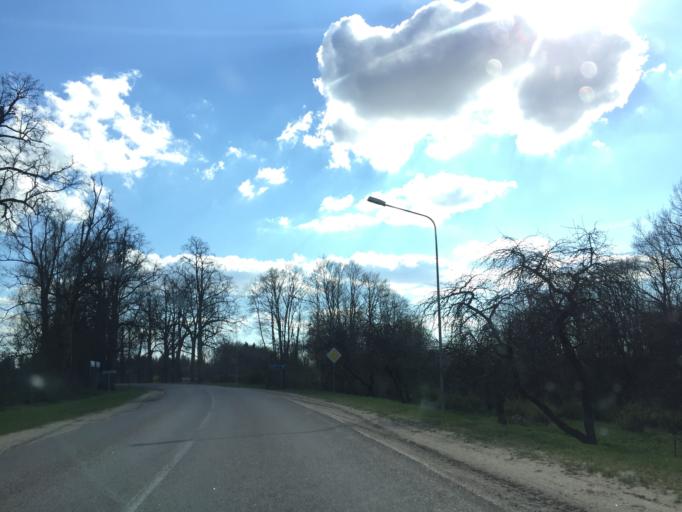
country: LV
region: Krimulda
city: Ragana
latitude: 57.3459
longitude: 24.6588
